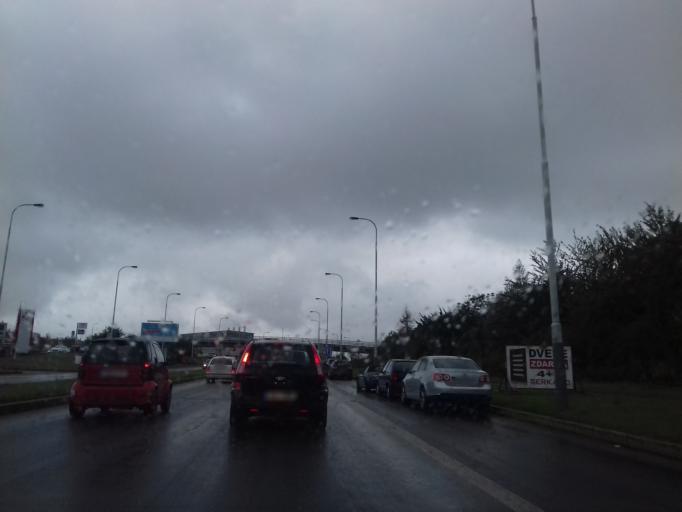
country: CZ
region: Praha
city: Branik
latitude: 50.0428
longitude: 14.3360
